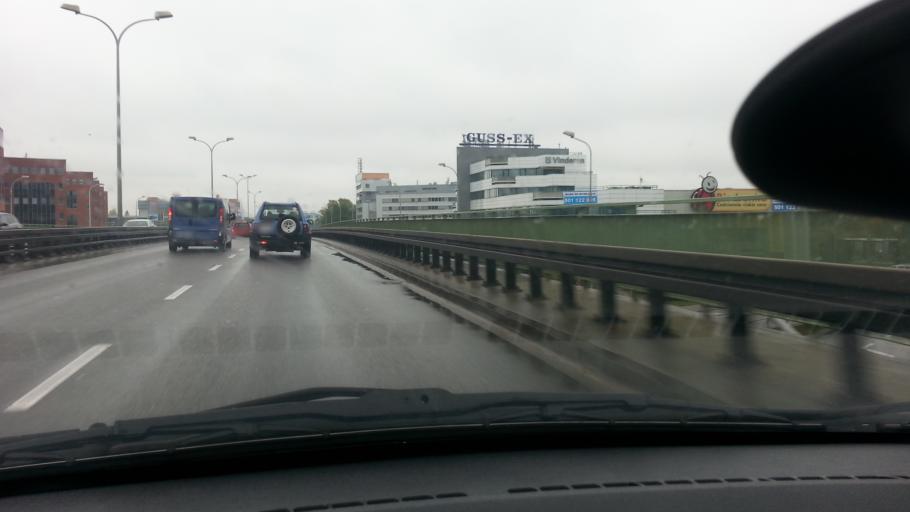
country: PL
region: Masovian Voivodeship
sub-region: Warszawa
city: Wlochy
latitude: 52.2010
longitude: 20.9362
